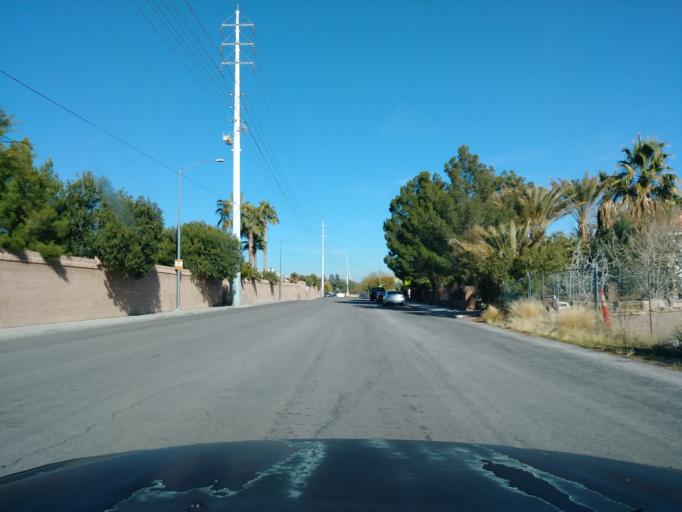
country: US
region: Nevada
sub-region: Clark County
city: Spring Valley
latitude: 36.1486
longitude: -115.2771
